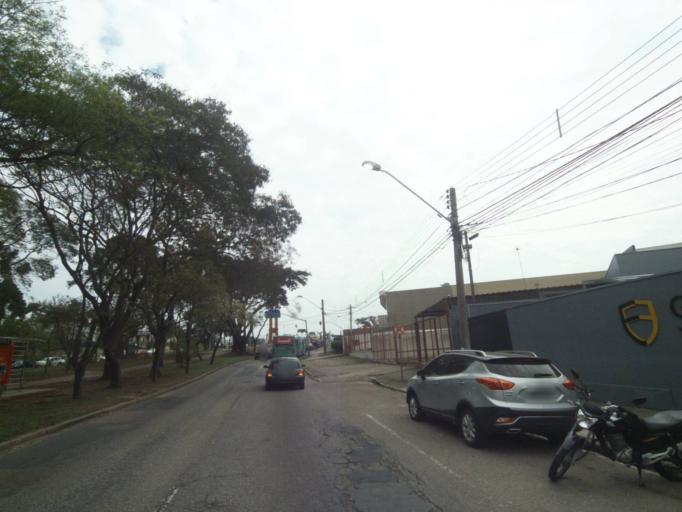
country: BR
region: Parana
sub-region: Curitiba
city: Curitiba
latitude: -25.4534
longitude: -49.3041
